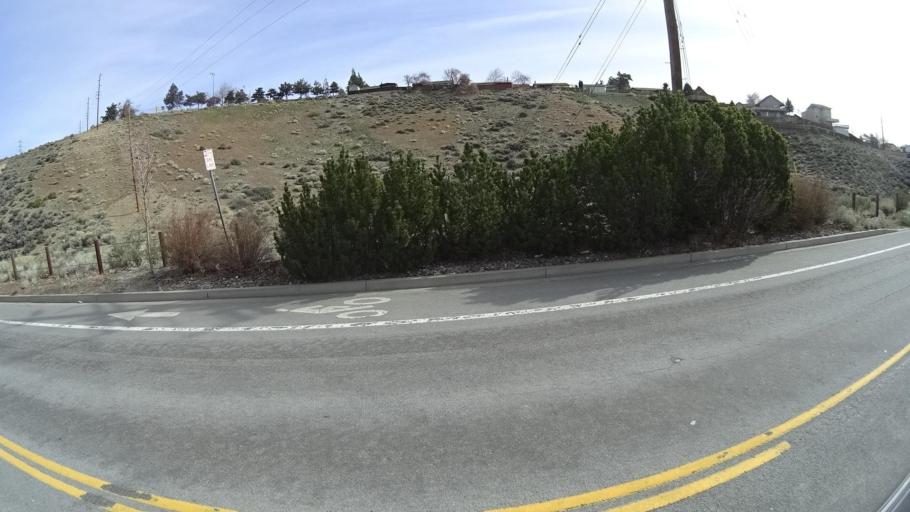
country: US
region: Nevada
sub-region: Washoe County
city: Reno
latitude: 39.5420
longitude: -119.8639
